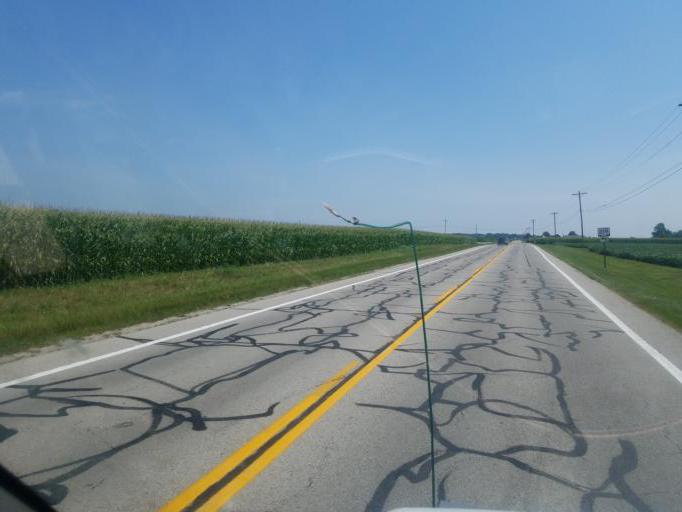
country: US
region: Ohio
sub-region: Mercer County
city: Celina
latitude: 40.4966
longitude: -84.4885
